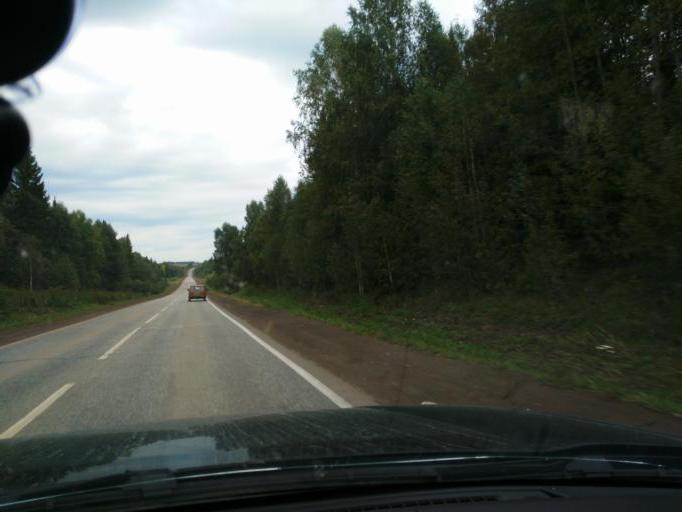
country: RU
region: Perm
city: Chernushka
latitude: 56.8025
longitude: 56.0664
